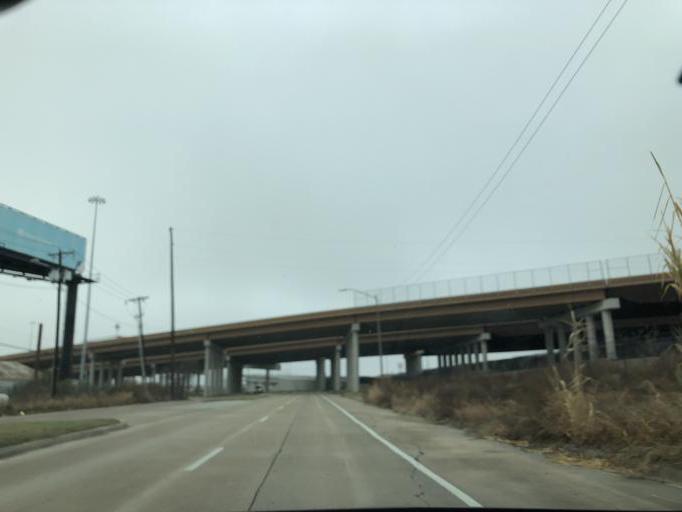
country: US
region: Texas
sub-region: Tarrant County
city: Haltom City
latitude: 32.8104
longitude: -97.3132
